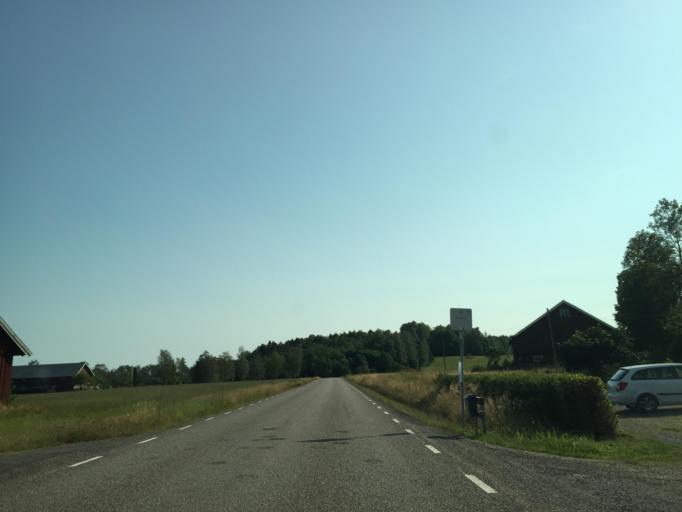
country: SE
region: Vaestra Goetaland
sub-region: Trollhattan
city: Sjuntorp
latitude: 58.2253
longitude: 12.1488
